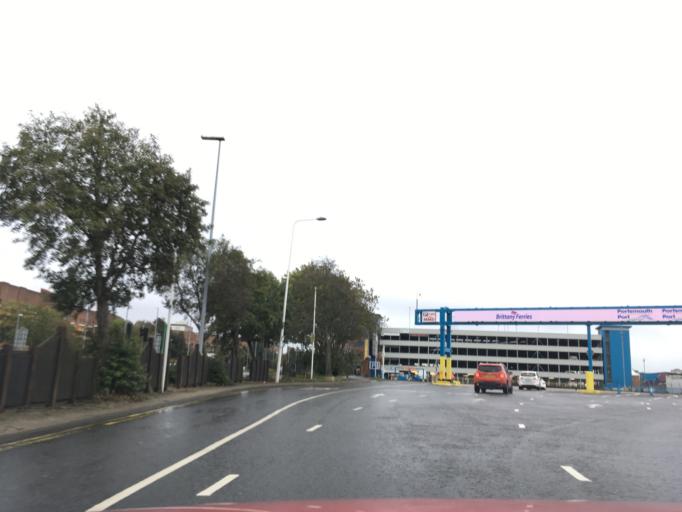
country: GB
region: England
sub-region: Portsmouth
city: Portsmouth
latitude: 50.8117
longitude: -1.0865
